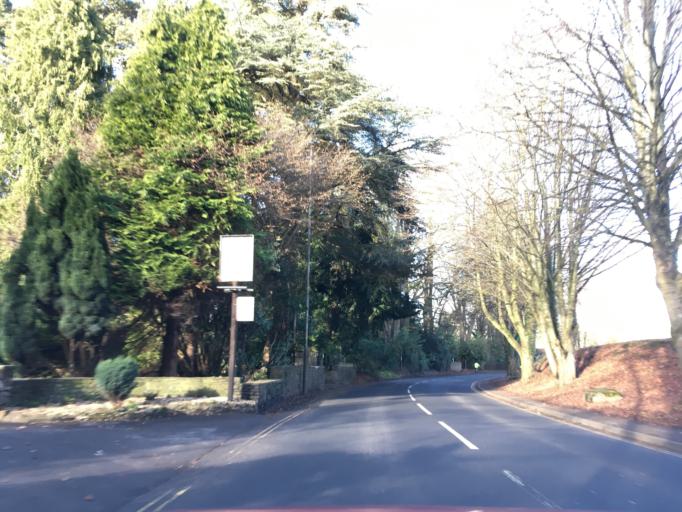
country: GB
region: Wales
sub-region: Monmouthshire
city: Usk
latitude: 51.7036
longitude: -2.9089
